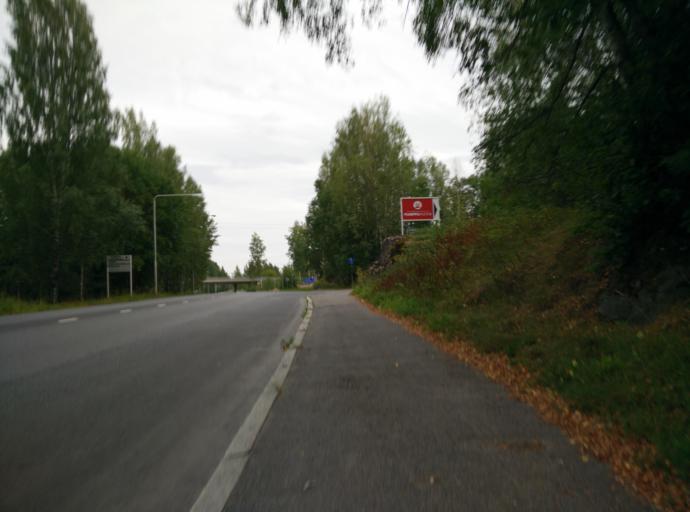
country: FI
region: Haeme
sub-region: Haemeenlinna
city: Haemeenlinna
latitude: 60.9835
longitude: 24.5021
